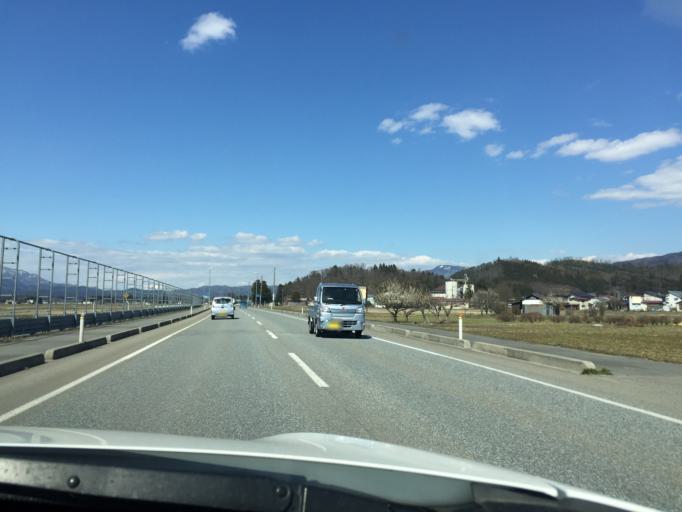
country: JP
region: Yamagata
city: Nagai
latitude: 38.1452
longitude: 140.0611
